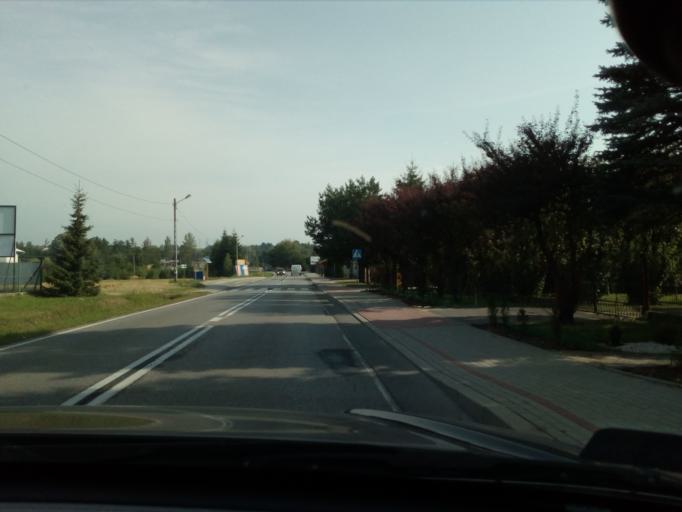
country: PL
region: Subcarpathian Voivodeship
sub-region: Powiat lancucki
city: Albigowa
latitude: 50.0362
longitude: 22.2298
